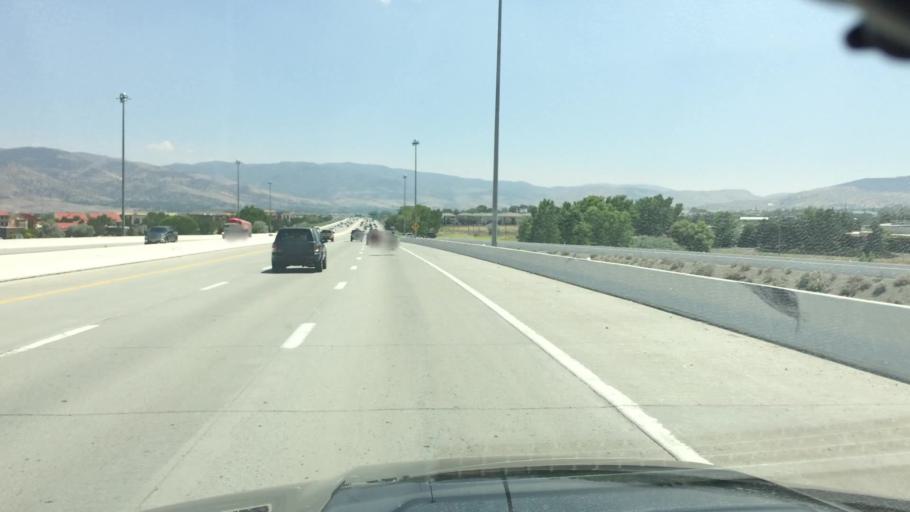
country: US
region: Nevada
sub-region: Washoe County
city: Sparks
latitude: 39.4381
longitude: -119.7649
